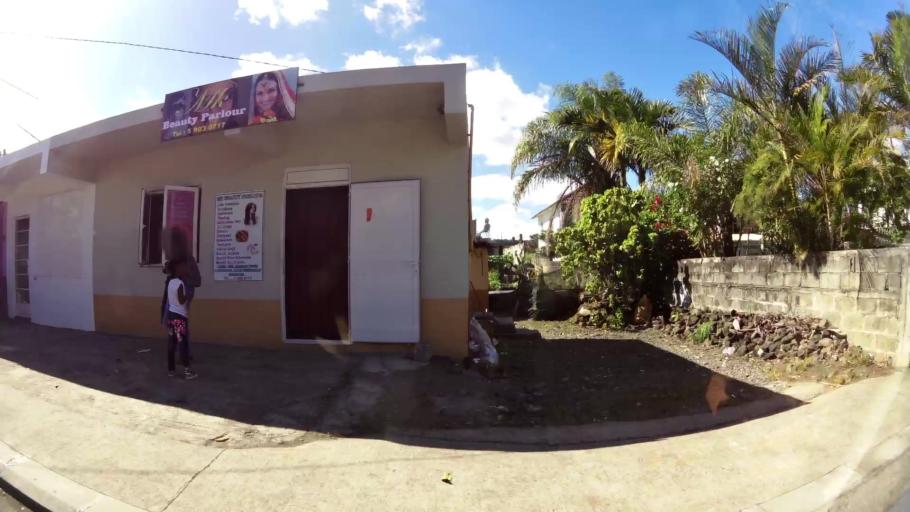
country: MU
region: Plaines Wilhems
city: Vacoas
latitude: -20.3268
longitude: 57.4859
